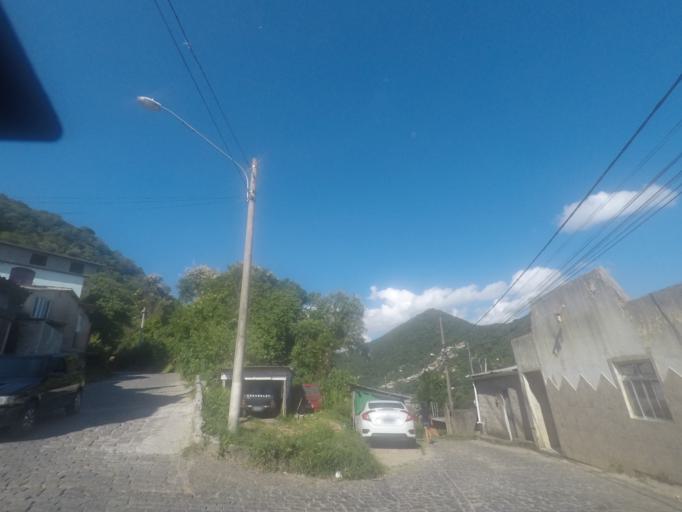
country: BR
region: Rio de Janeiro
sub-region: Petropolis
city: Petropolis
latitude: -22.5463
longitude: -43.1999
